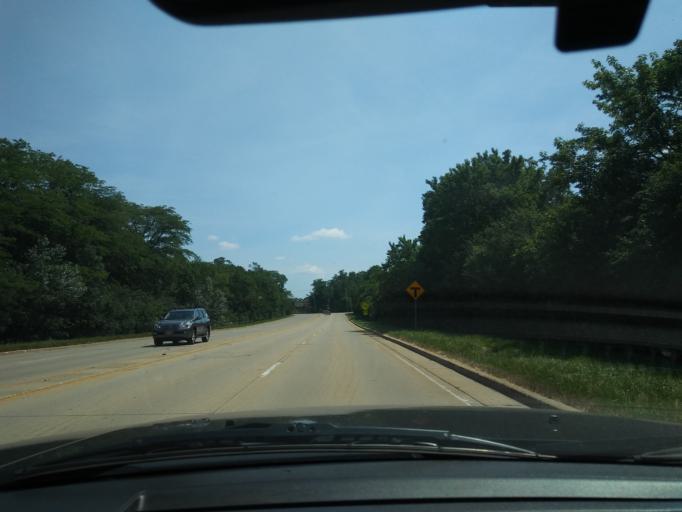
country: US
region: Illinois
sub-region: Cook County
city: Oak Forest
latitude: 41.6266
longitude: -87.7764
